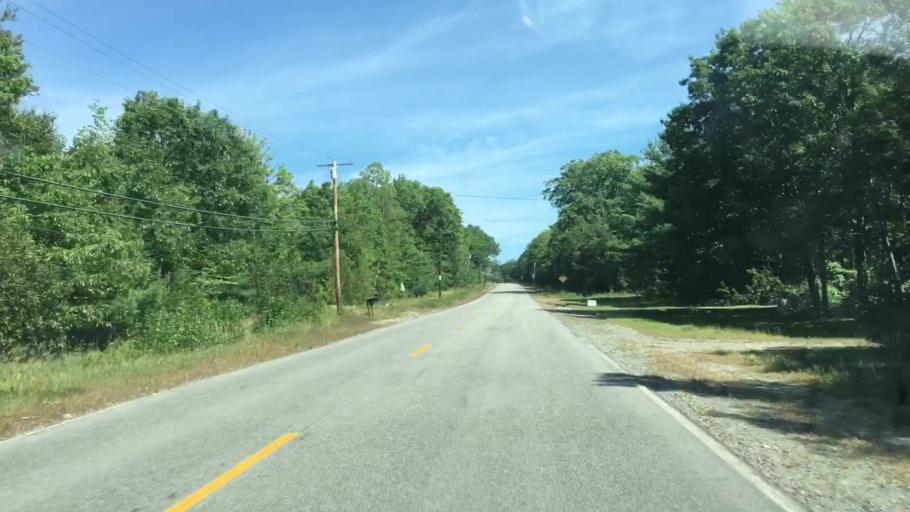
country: US
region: Maine
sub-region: Penobscot County
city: Bradford
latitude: 45.1762
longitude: -68.8622
